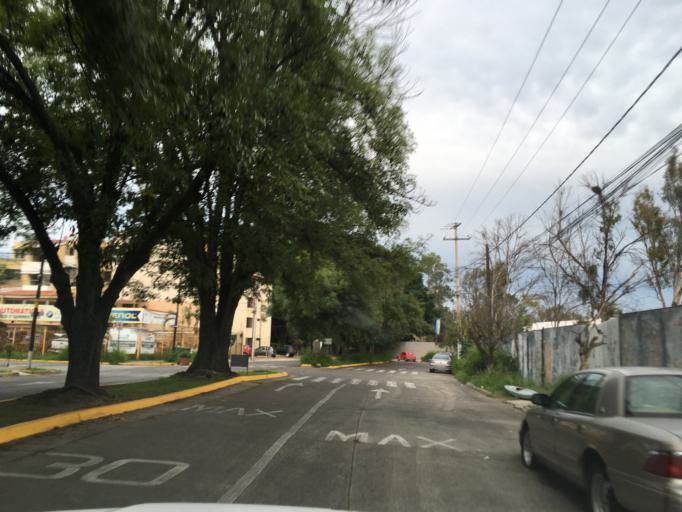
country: MX
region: Jalisco
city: Guadalajara
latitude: 20.6566
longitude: -103.3976
